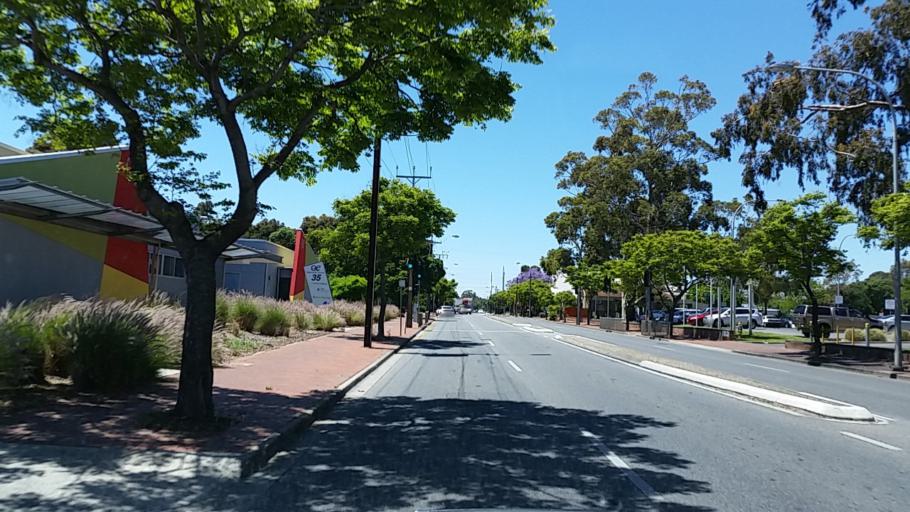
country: AU
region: South Australia
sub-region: Charles Sturt
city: Woodville West
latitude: -34.8830
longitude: 138.5332
